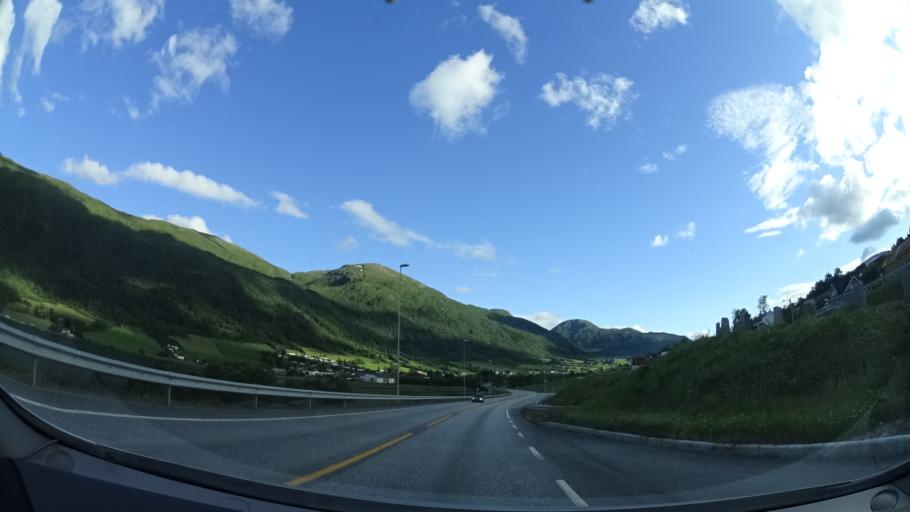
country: NO
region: More og Romsdal
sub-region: Gjemnes
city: Batnfjordsora
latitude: 62.9003
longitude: 7.6763
